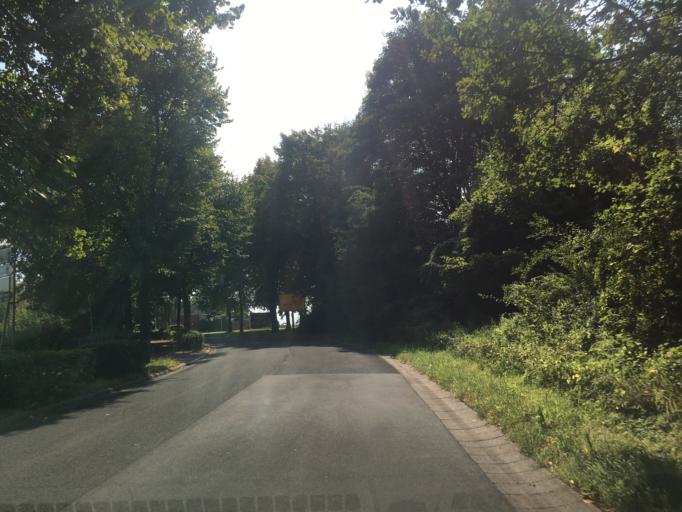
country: DE
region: North Rhine-Westphalia
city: Selm
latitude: 51.6682
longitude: 7.4567
